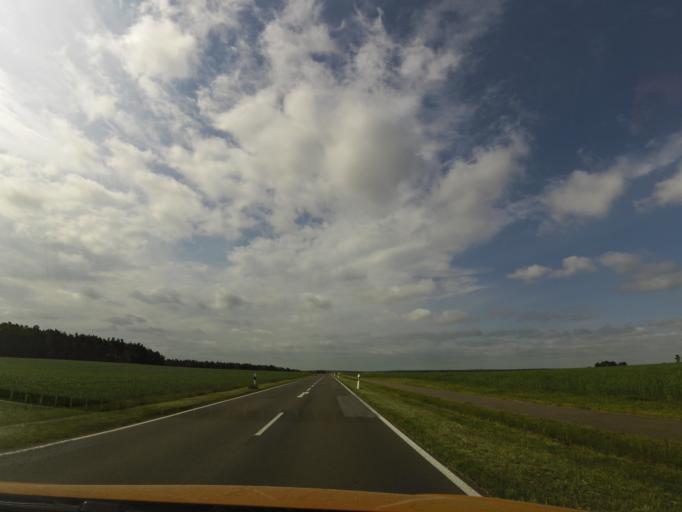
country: DE
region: Brandenburg
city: Belzig
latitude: 52.0831
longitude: 12.5338
